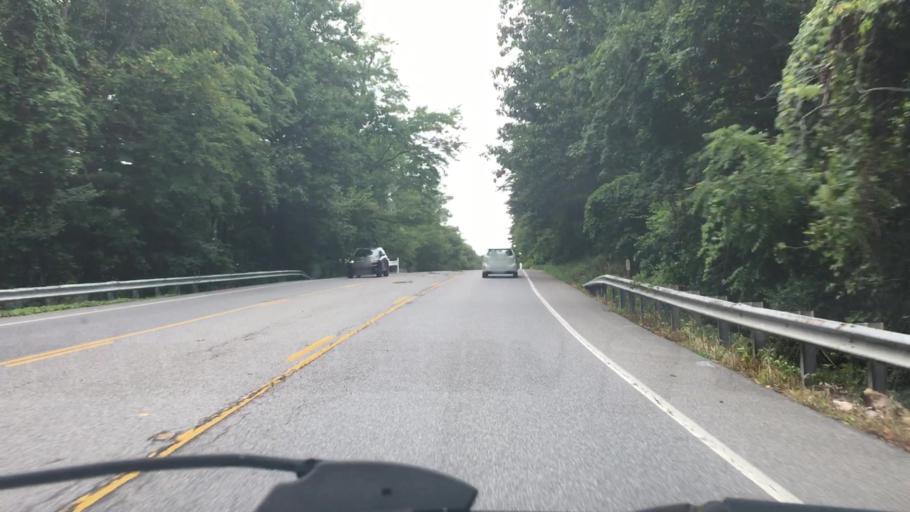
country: US
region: Maryland
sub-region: Anne Arundel County
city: Arden on the Severn
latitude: 39.0854
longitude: -76.6028
